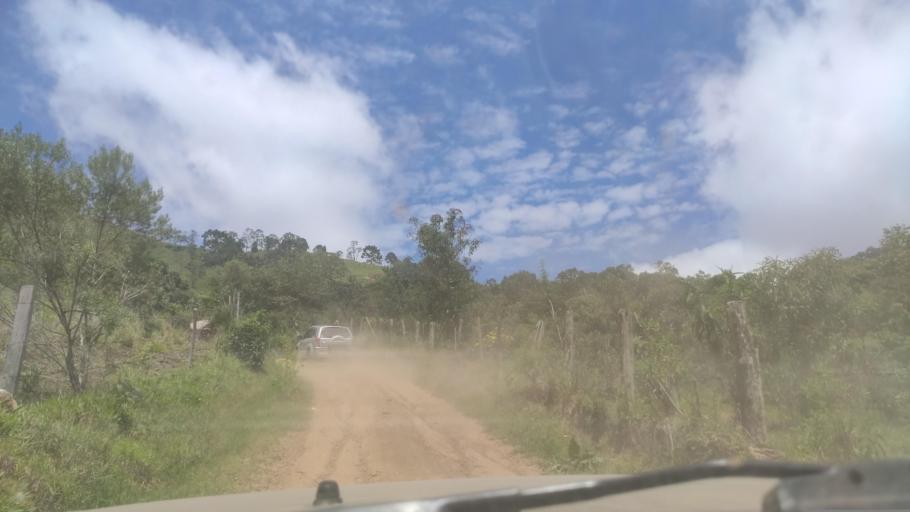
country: BR
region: Minas Gerais
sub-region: Cambui
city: Cambui
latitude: -22.6687
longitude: -45.9440
